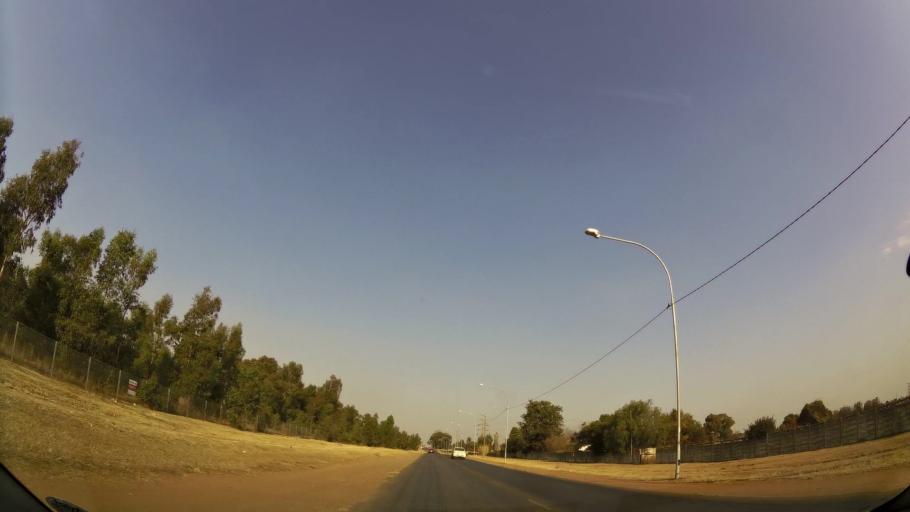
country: ZA
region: Gauteng
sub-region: Ekurhuleni Metropolitan Municipality
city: Benoni
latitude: -26.1118
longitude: 28.3718
